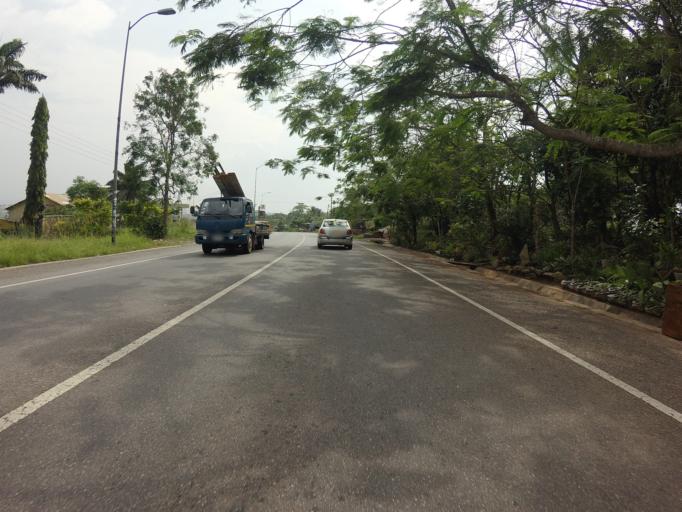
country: GH
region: Eastern
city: Aburi
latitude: 5.8315
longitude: -0.1840
